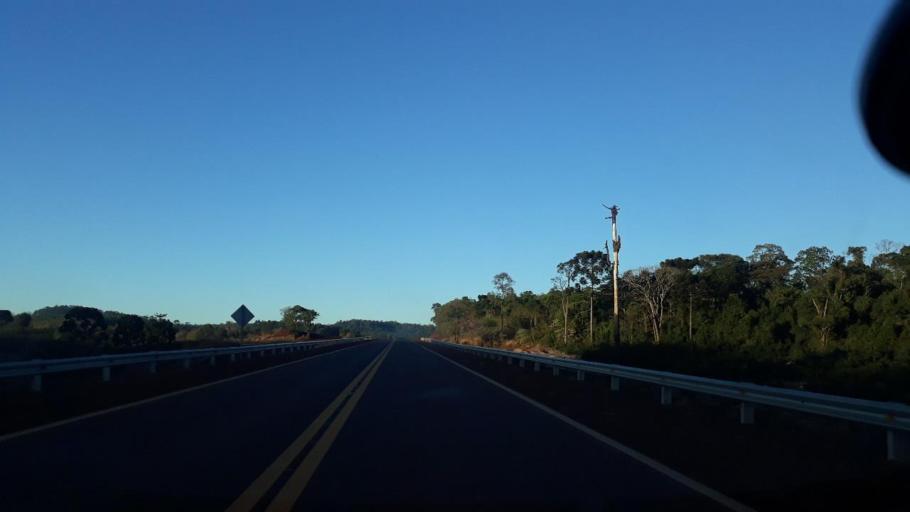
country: AR
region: Misiones
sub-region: Departamento de San Pedro
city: San Pedro
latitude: -26.5421
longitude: -53.9598
